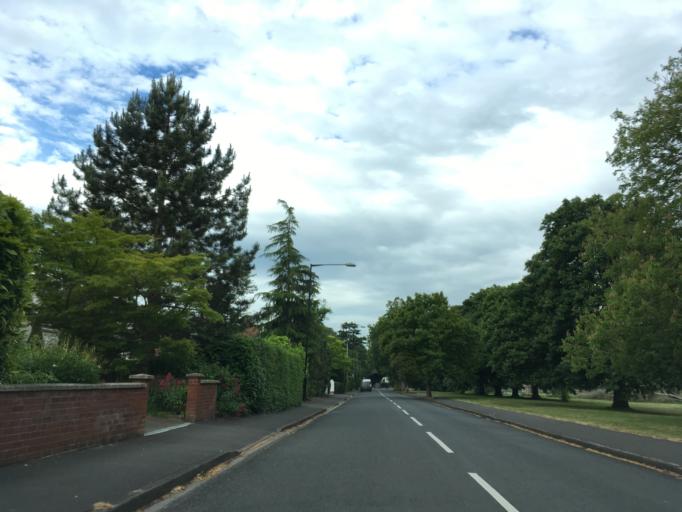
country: GB
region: England
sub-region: North Somerset
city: Easton-in-Gordano
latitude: 51.4823
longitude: -2.6457
